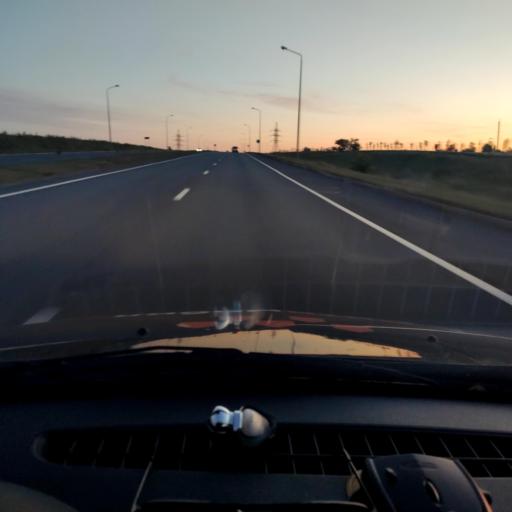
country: RU
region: Belgorod
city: Staryy Oskol
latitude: 51.3241
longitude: 37.7178
